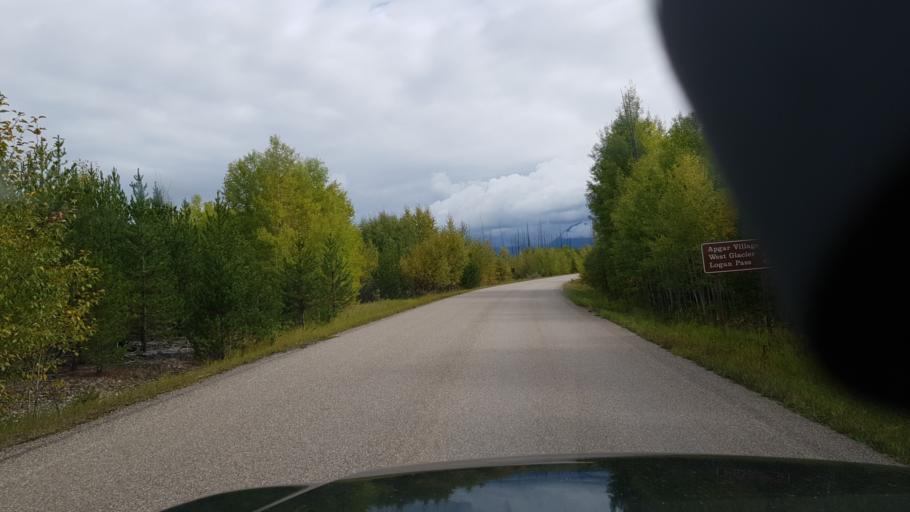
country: US
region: Montana
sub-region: Flathead County
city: Columbia Falls
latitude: 48.6279
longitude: -114.1239
